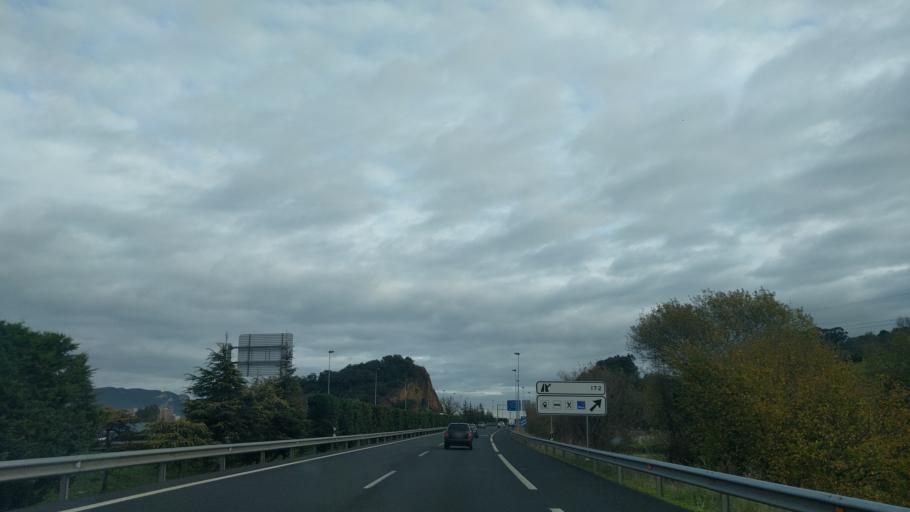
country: ES
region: Cantabria
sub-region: Provincia de Cantabria
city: Colindres
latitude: 43.3963
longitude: -3.4418
